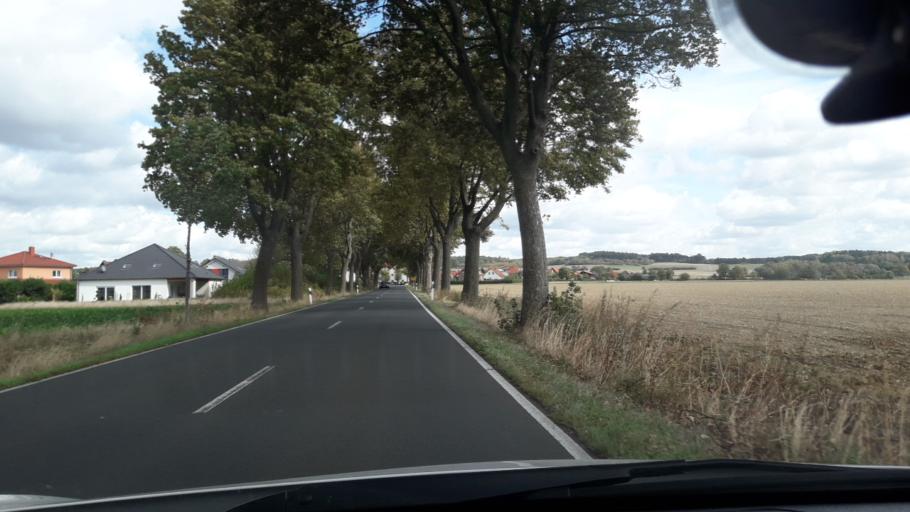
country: DE
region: Lower Saxony
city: Alt Wallmoden
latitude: 52.0485
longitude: 10.3242
